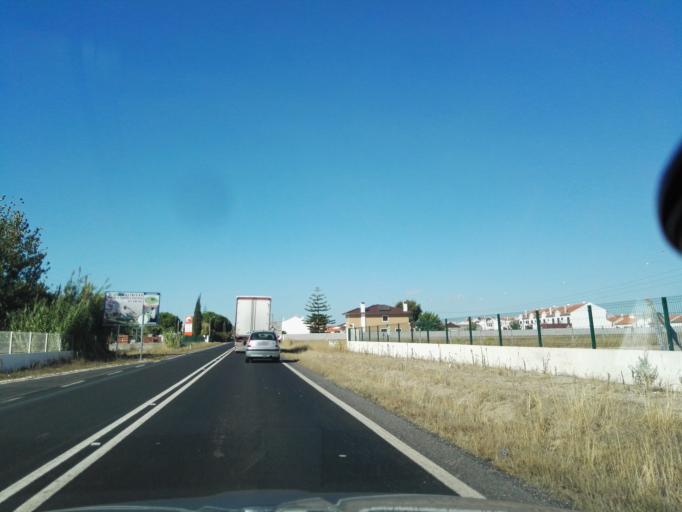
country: PT
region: Santarem
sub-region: Benavente
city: Samora Correia
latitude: 38.9165
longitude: -8.8816
